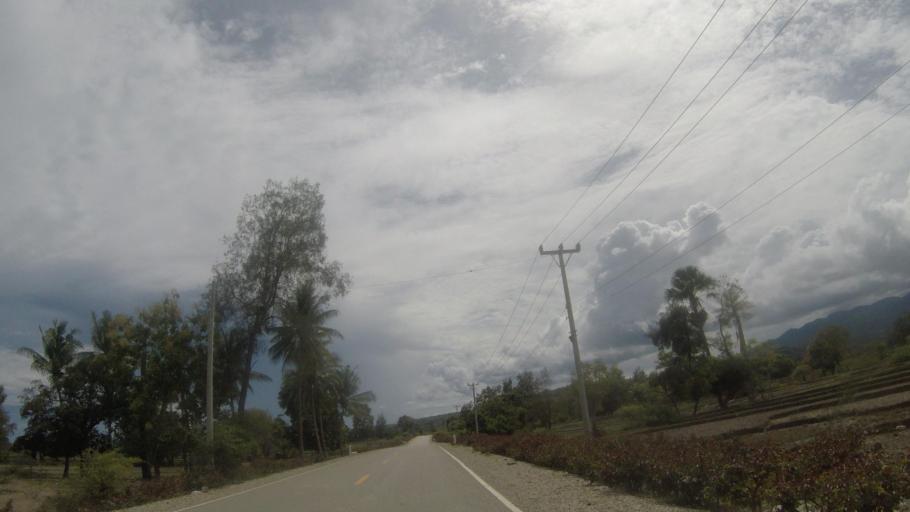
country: TL
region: Baucau
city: Baucau
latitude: -8.4801
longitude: 126.5781
